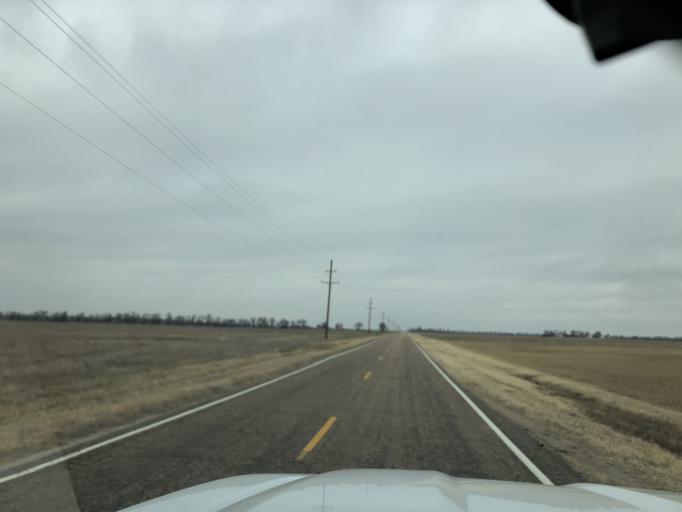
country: US
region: Kansas
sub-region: Rice County
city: Sterling
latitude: 38.0280
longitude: -98.2521
